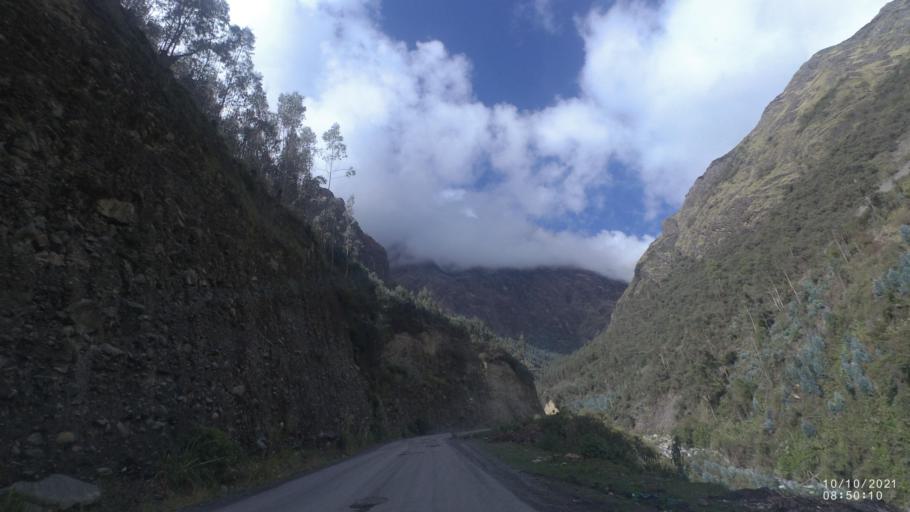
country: BO
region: La Paz
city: Quime
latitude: -16.9808
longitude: -67.2259
